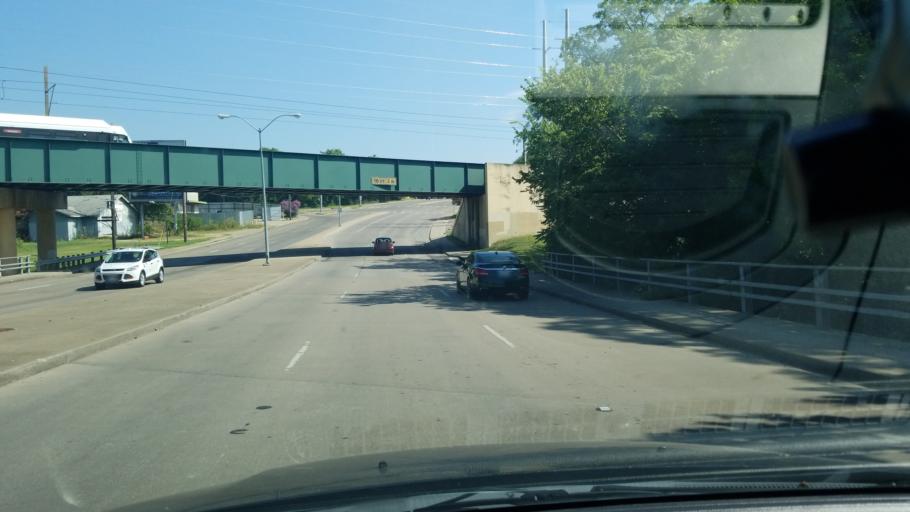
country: US
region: Texas
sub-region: Dallas County
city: Dallas
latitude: 32.7470
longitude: -96.7995
